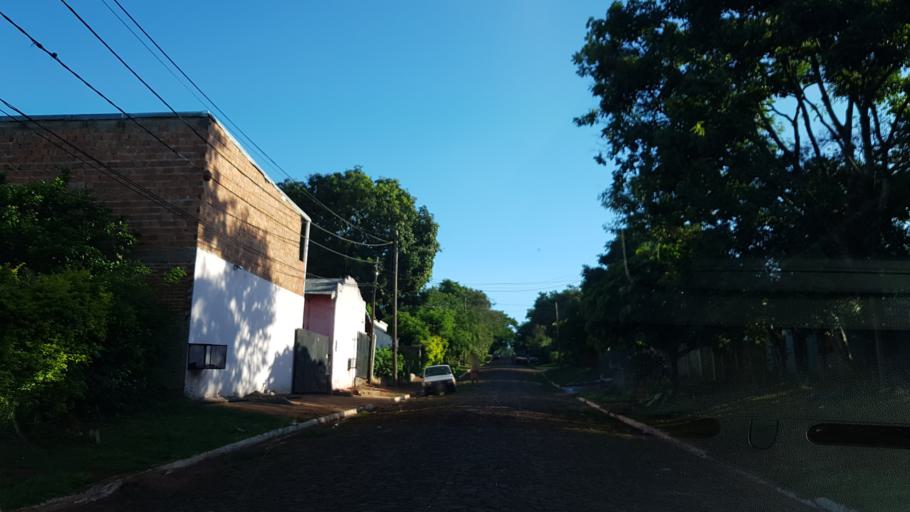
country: AR
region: Misiones
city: Puerto Libertad
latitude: -25.9191
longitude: -54.5869
